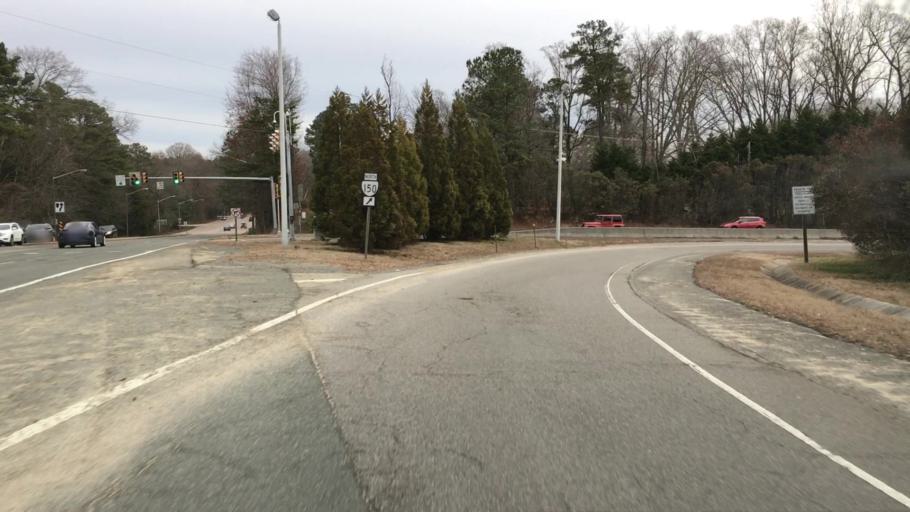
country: US
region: Virginia
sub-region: Chesterfield County
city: Bon Air
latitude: 37.5463
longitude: -77.5523
